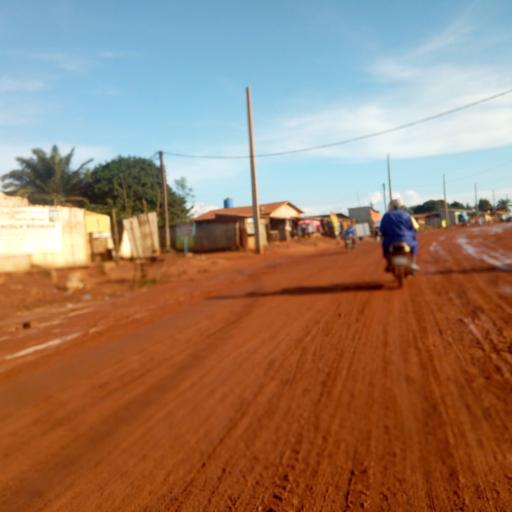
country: BJ
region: Atlantique
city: Hevie
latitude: 6.4018
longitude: 2.2685
